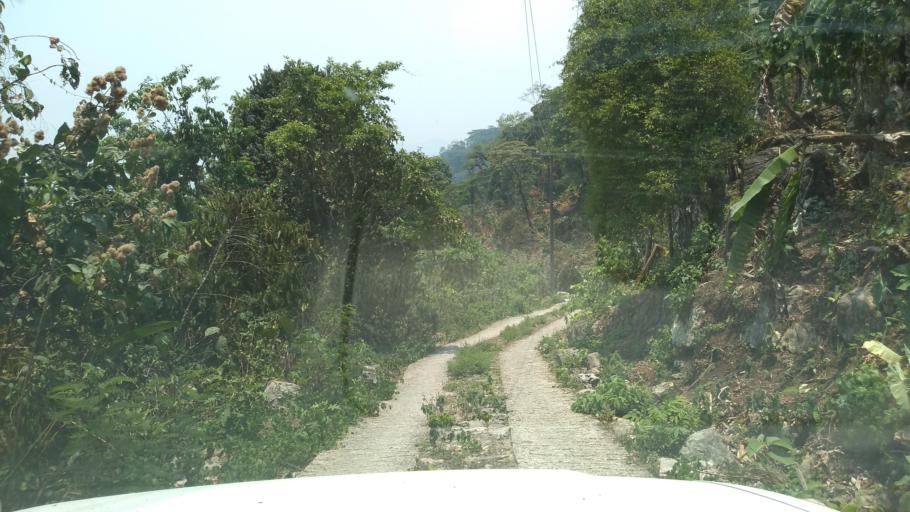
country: MX
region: Veracruz
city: Motzorongo
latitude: 18.6010
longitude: -96.7493
